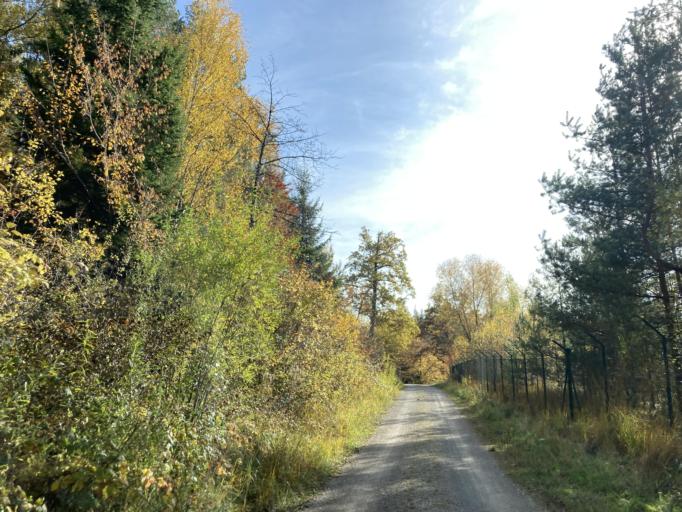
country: DE
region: Baden-Wuerttemberg
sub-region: Tuebingen Region
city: Bodelshausen
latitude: 48.4135
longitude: 8.9579
